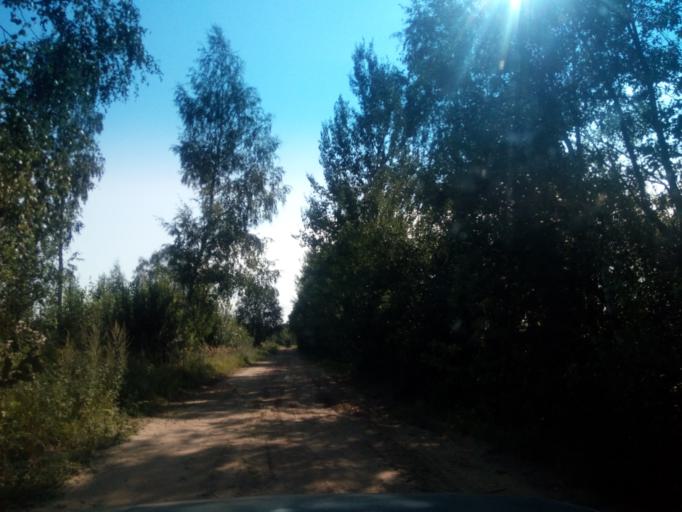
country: BY
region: Vitebsk
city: Dzisna
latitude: 55.6471
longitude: 28.2639
